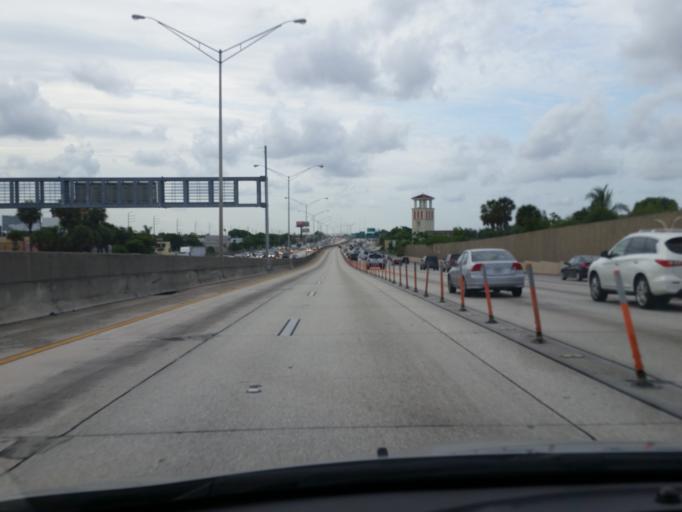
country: US
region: Florida
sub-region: Miami-Dade County
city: Pinewood
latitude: 25.8770
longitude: -80.2089
